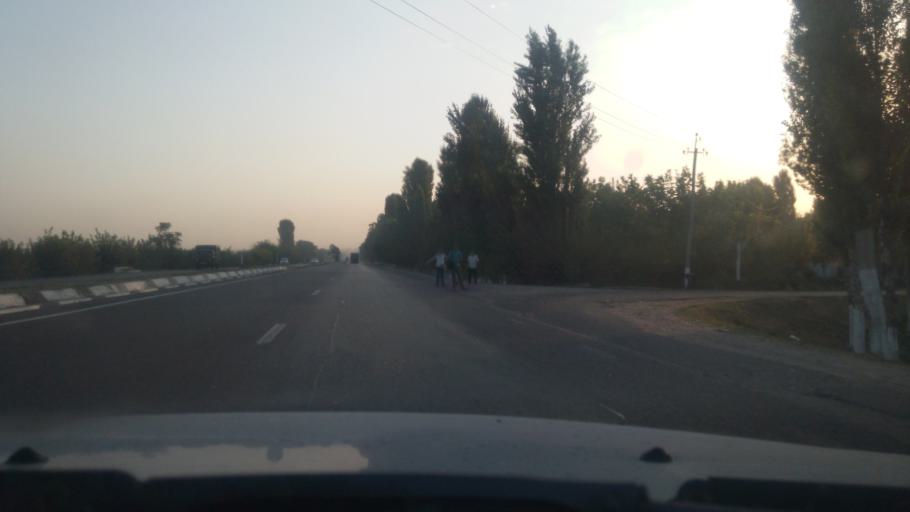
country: UZ
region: Toshkent
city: Yangiyul
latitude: 41.1771
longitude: 69.0745
